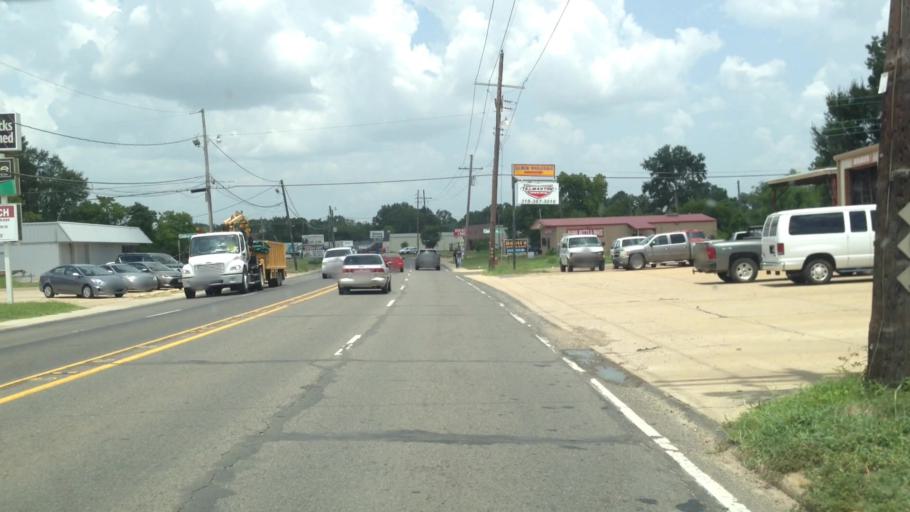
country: US
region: Louisiana
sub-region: Ouachita Parish
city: West Monroe
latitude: 32.5155
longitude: -92.1381
